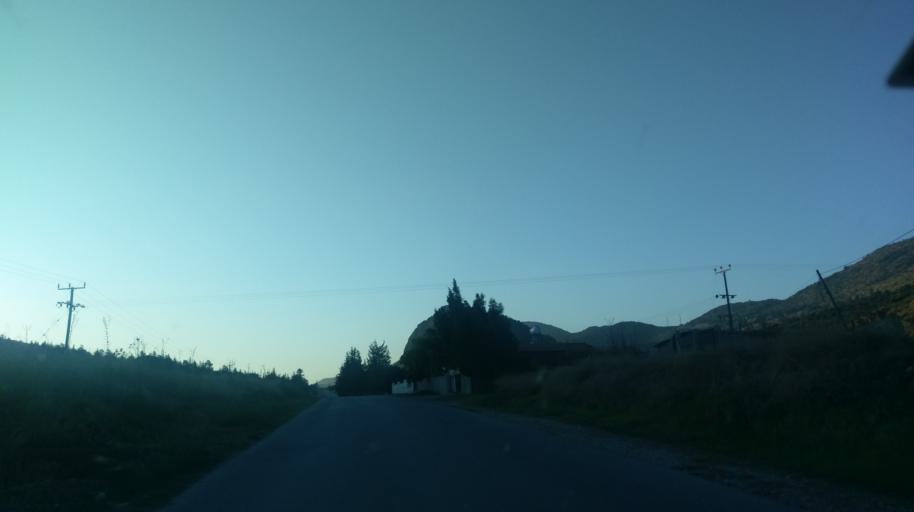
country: CY
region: Lefkosia
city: Nicosia
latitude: 35.2693
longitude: 33.4874
